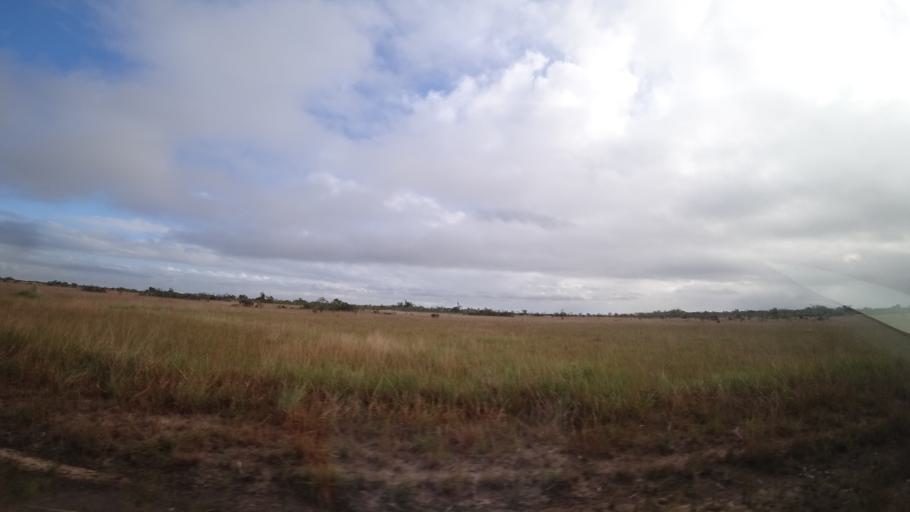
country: MZ
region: Sofala
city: Beira
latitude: -19.6146
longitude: 35.0665
